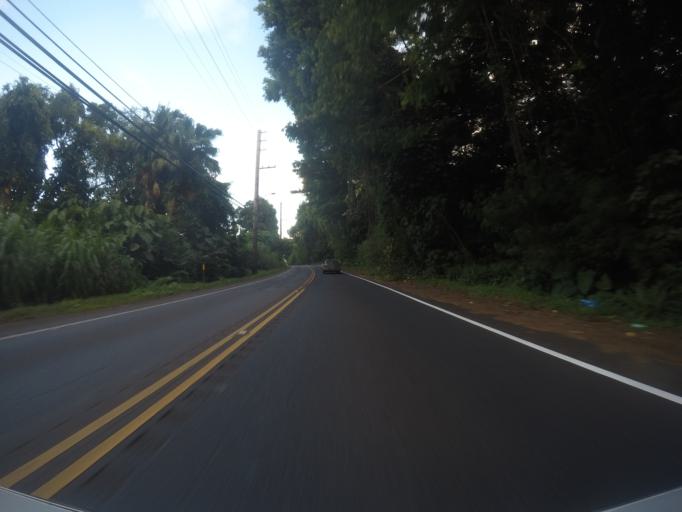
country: US
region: Hawaii
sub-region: Honolulu County
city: Kahalu'u
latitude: 21.5043
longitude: -157.8558
